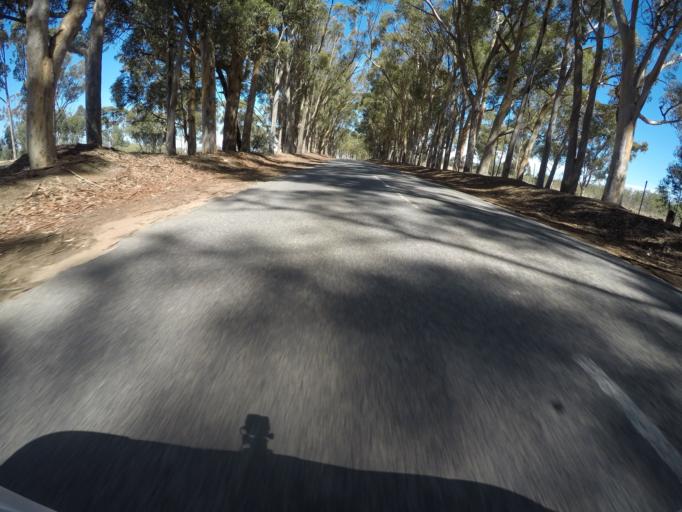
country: ZA
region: Western Cape
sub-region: City of Cape Town
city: Sunset Beach
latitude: -33.7573
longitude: 18.5542
